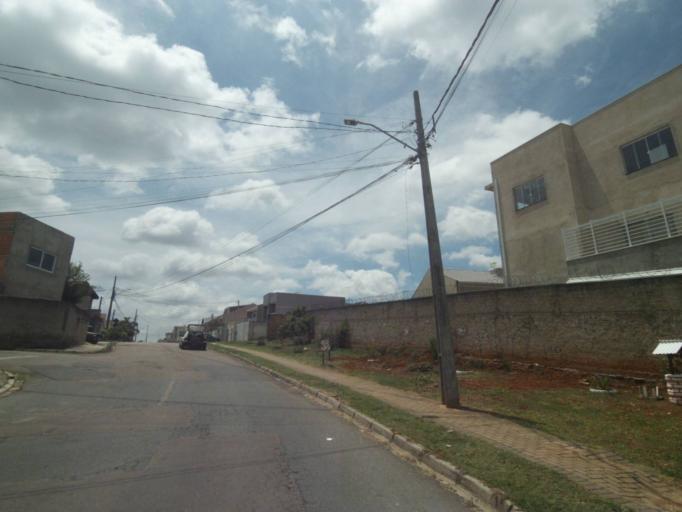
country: BR
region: Parana
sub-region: Curitiba
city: Curitiba
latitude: -25.4603
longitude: -49.3489
